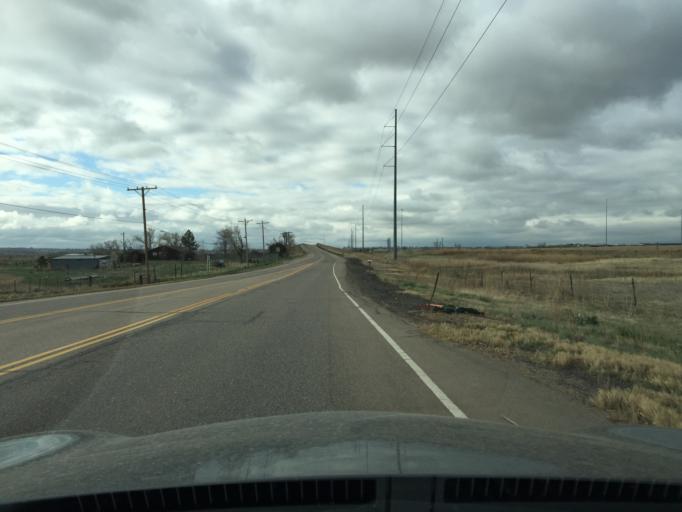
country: US
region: Colorado
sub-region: Boulder County
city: Erie
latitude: 39.9849
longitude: -104.9784
